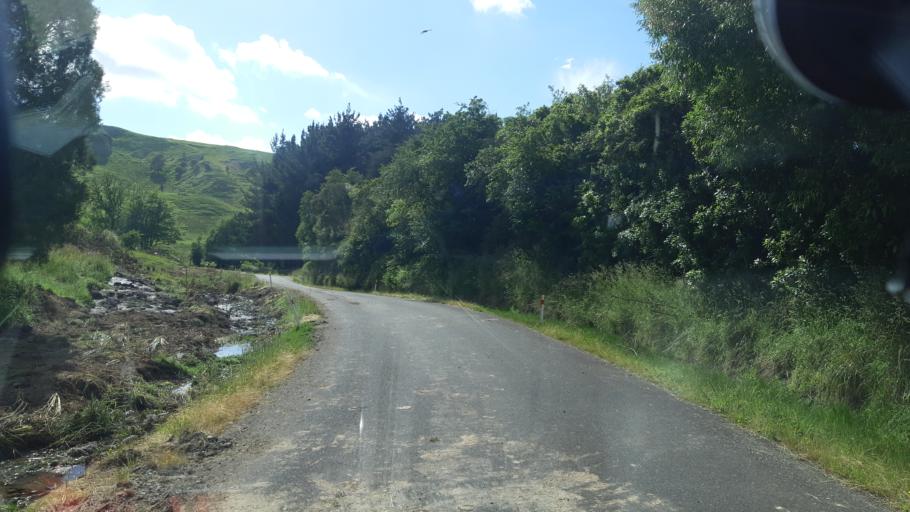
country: NZ
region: Manawatu-Wanganui
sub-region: Rangitikei District
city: Bulls
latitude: -39.9559
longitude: 175.5068
